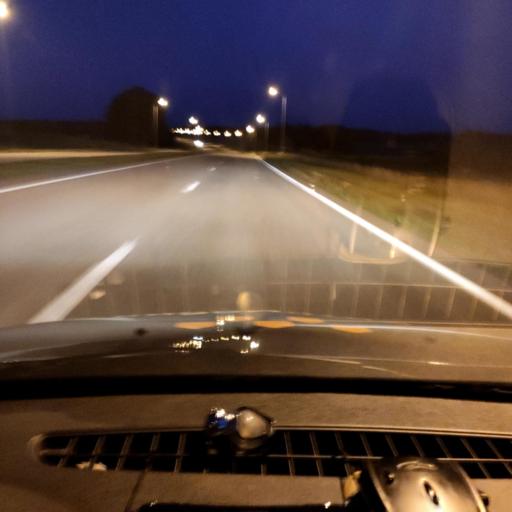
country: RU
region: Belgorod
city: Skorodnoye
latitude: 51.0437
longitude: 37.2043
